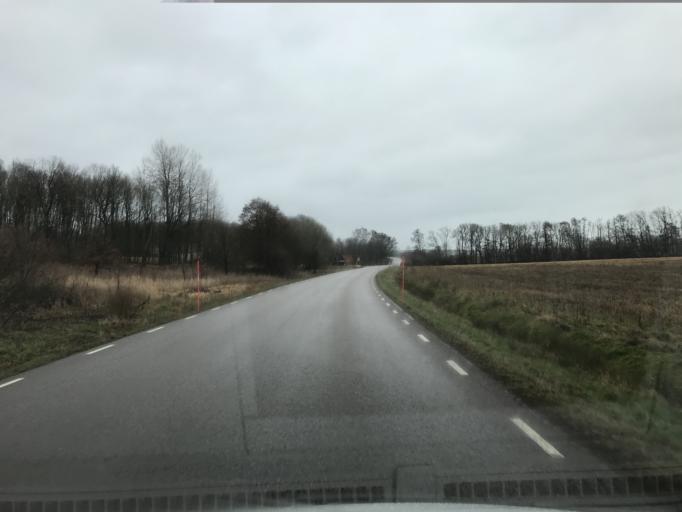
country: SE
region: Skane
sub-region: Bastads Kommun
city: Forslov
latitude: 56.3377
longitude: 12.8814
